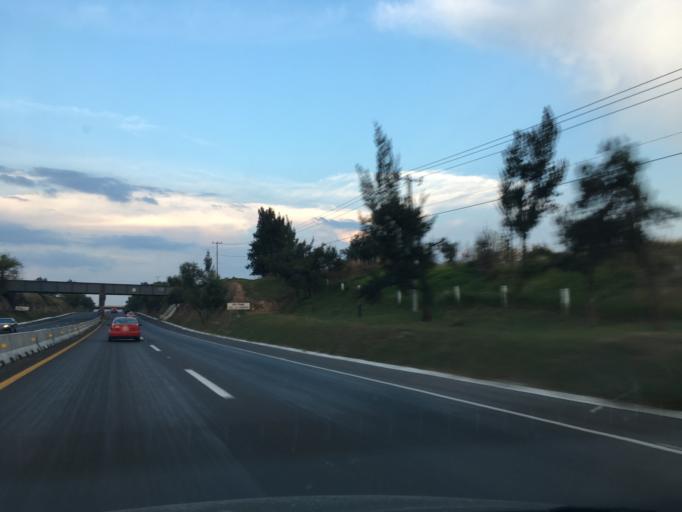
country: MX
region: Michoacan
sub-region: Morelia
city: Morelos
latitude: 19.6610
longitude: -101.2355
